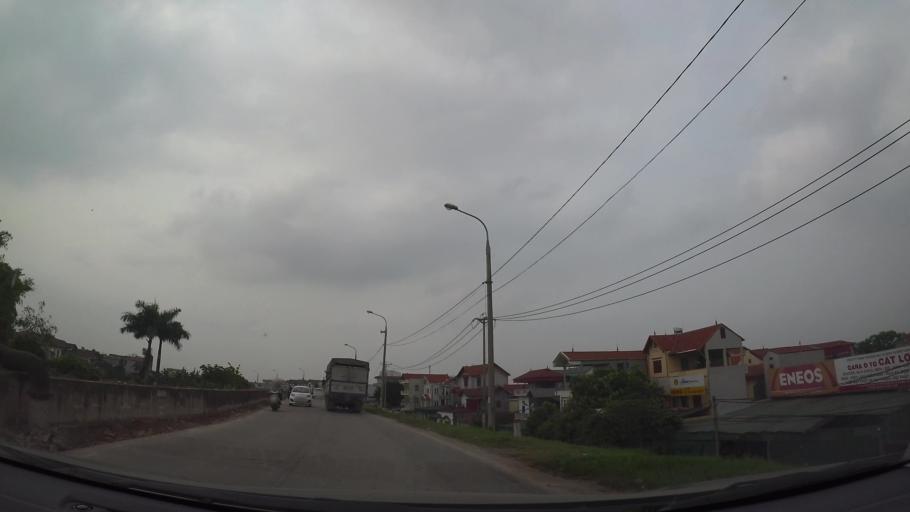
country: VN
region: Ha Noi
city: Trau Quy
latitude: 21.0057
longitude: 105.9075
